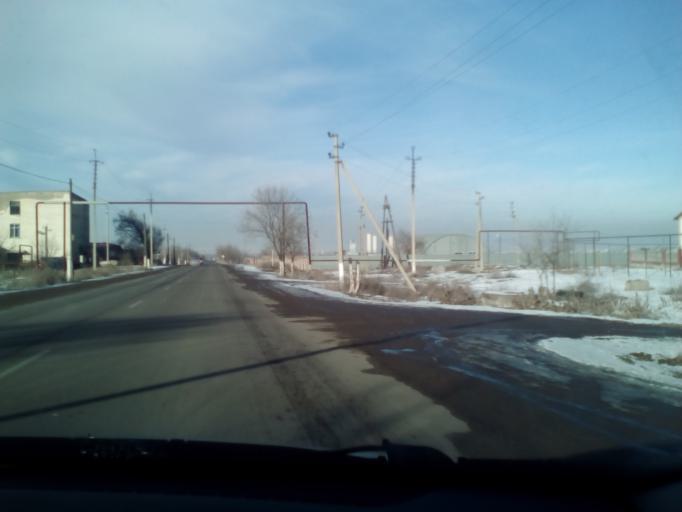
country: KZ
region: Almaty Oblysy
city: Burunday
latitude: 43.1914
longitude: 76.4148
